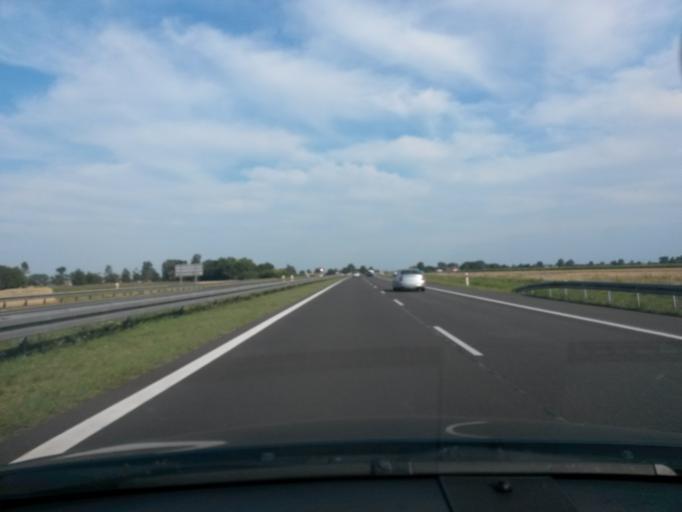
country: PL
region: Greater Poland Voivodeship
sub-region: Powiat slupecki
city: Slupca
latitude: 52.2415
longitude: 17.8749
